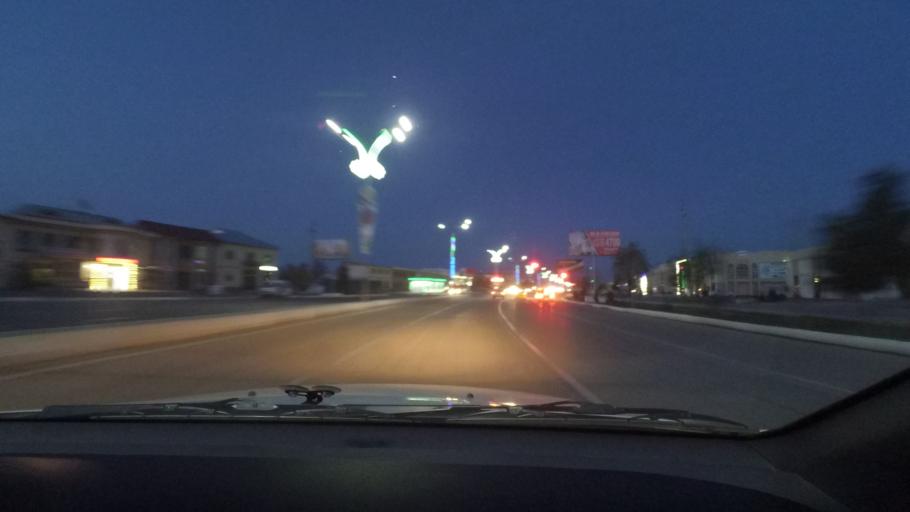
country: UZ
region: Bukhara
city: Bukhara
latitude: 39.7834
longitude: 64.4143
